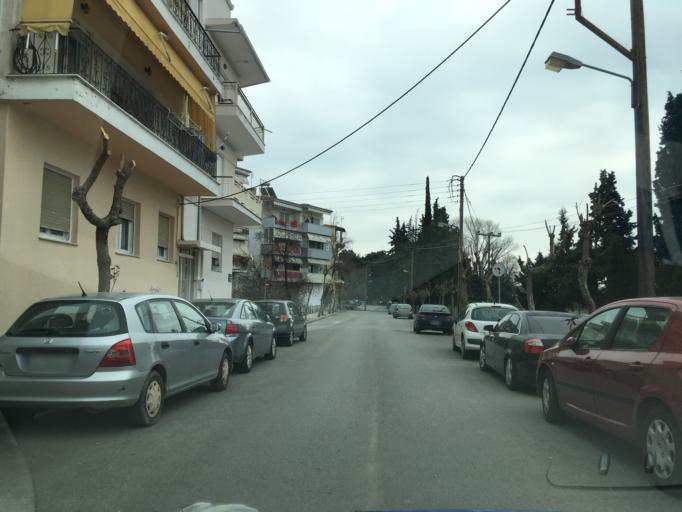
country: GR
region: West Macedonia
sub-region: Nomos Kozanis
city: Kozani
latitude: 40.2955
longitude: 21.7904
